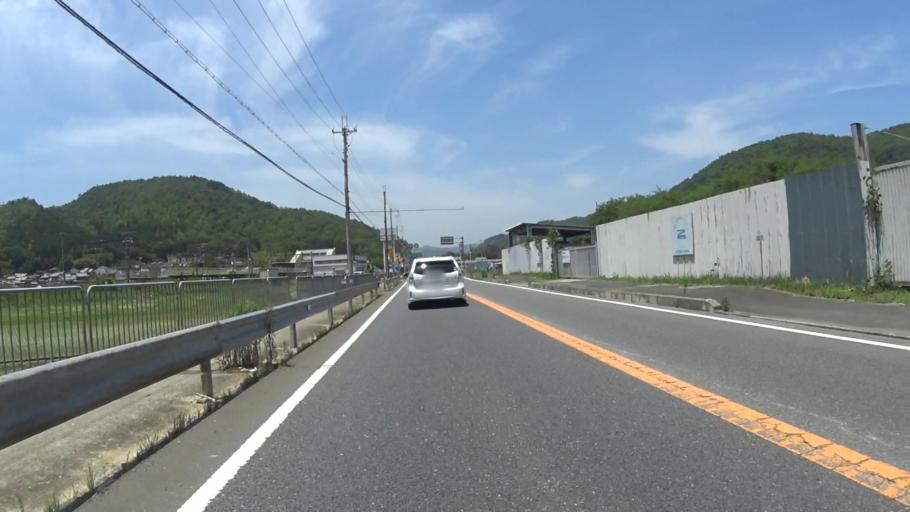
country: JP
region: Kyoto
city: Kameoka
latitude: 35.0910
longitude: 135.5003
